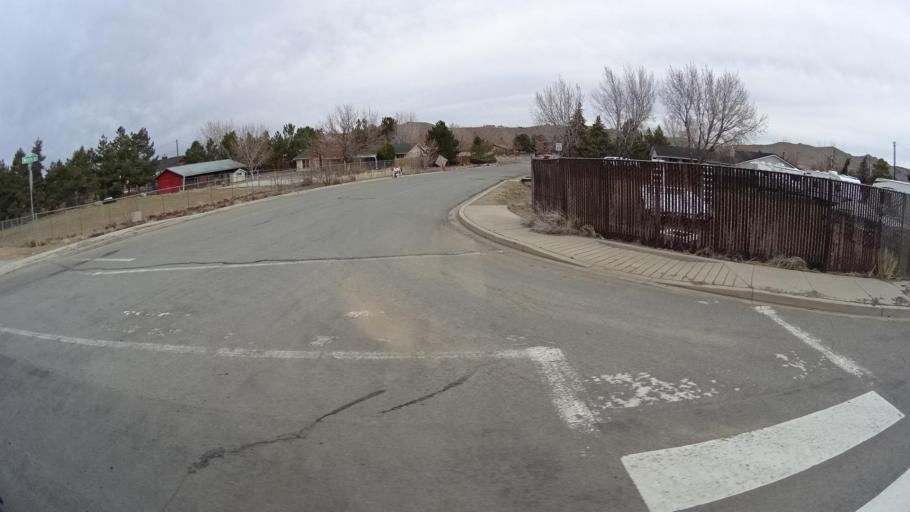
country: US
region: Nevada
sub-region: Washoe County
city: Golden Valley
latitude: 39.6076
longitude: -119.8324
